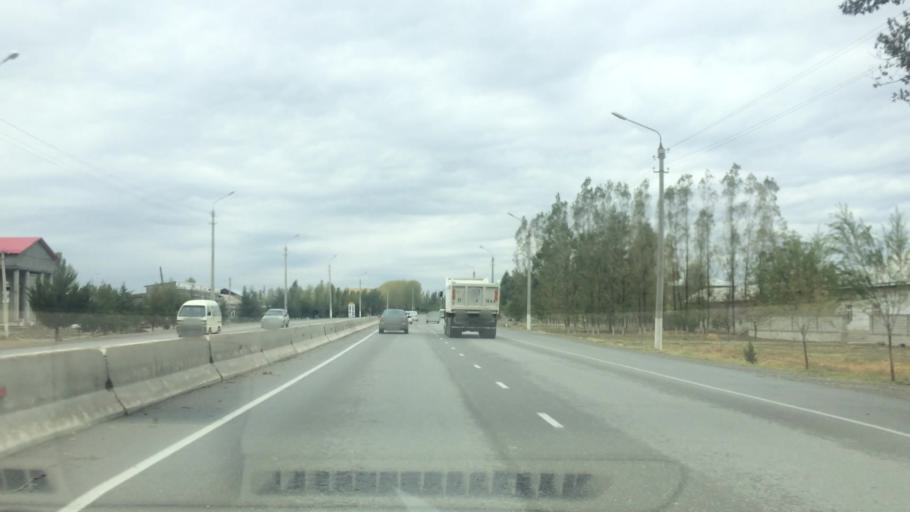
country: UZ
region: Jizzax
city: Jizzax
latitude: 39.9923
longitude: 67.5843
